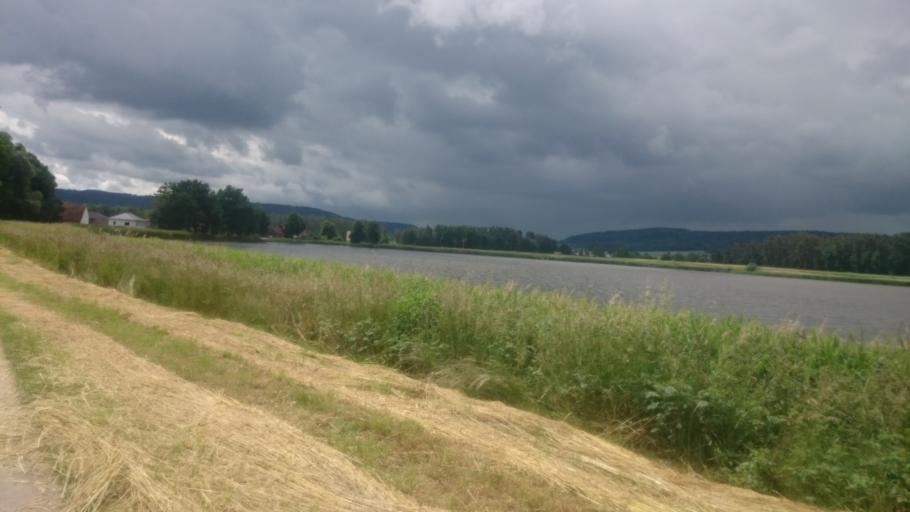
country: DE
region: Bavaria
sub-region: Upper Palatinate
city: Freystadt
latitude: 49.1527
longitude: 11.3204
